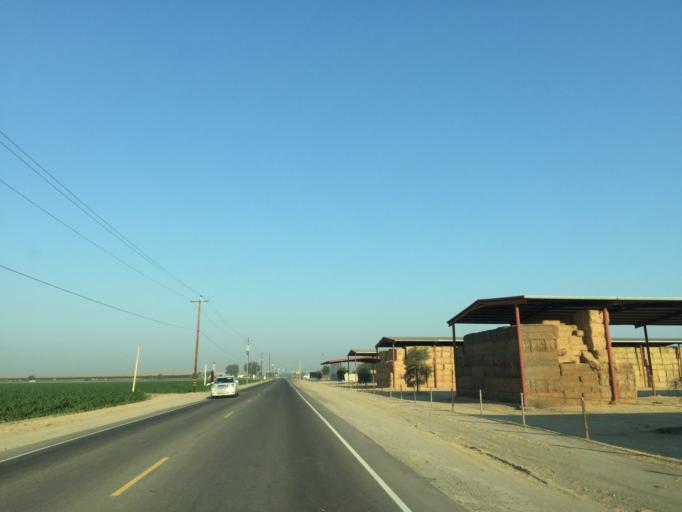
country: US
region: California
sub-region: Tulare County
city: London
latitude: 36.4585
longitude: -119.3892
